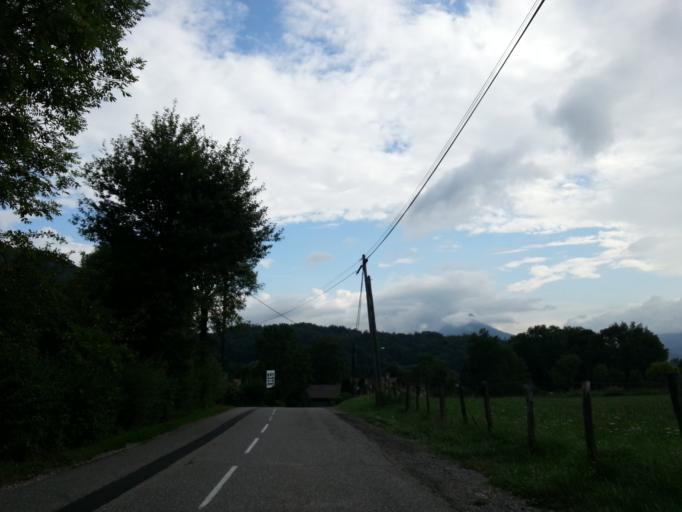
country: FR
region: Rhone-Alpes
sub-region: Departement de la Haute-Savoie
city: Menthon-Saint-Bernard
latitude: 45.8726
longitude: 6.2122
